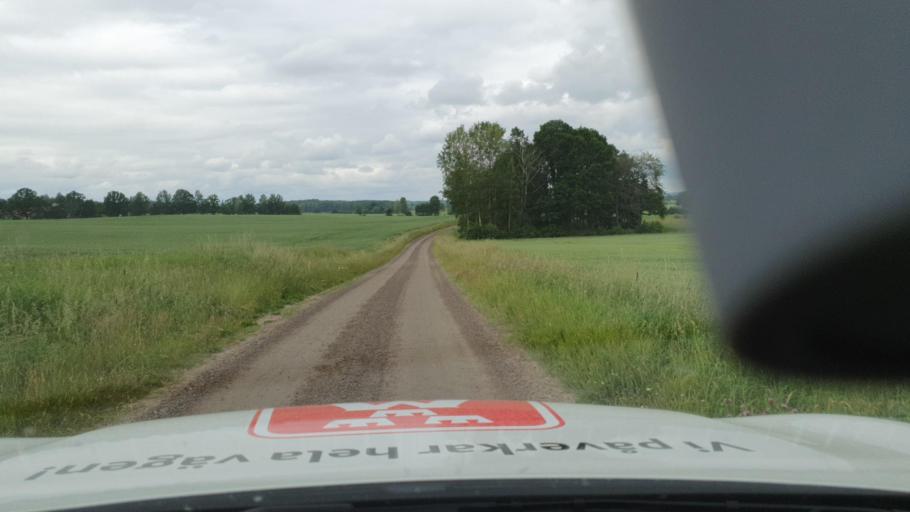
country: SE
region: Vaestra Goetaland
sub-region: Hjo Kommun
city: Hjo
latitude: 58.1784
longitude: 14.1724
